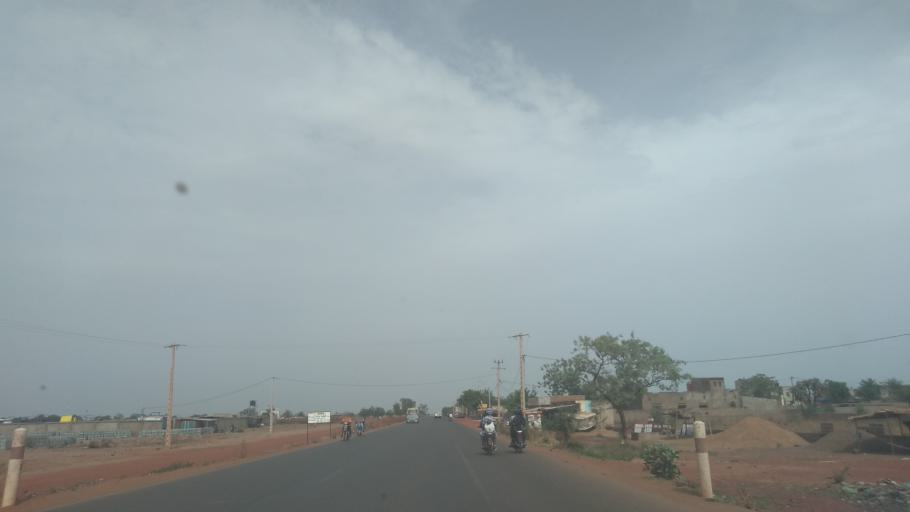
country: ML
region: Bamako
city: Bamako
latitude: 12.5840
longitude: -7.8229
